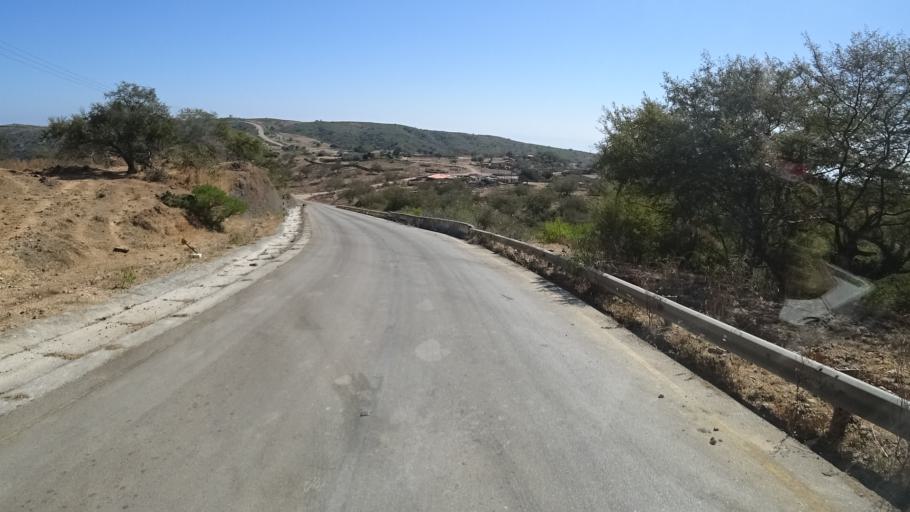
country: YE
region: Al Mahrah
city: Hawf
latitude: 16.7600
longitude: 53.3390
